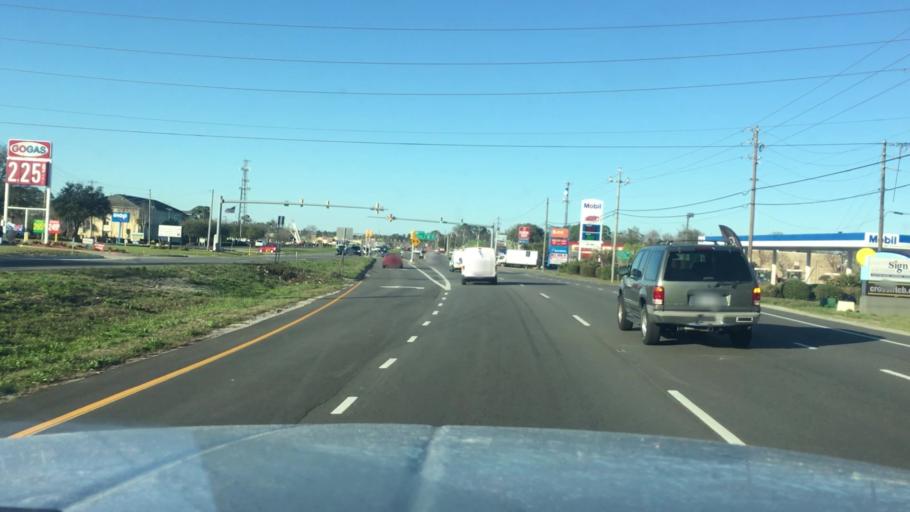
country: US
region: North Carolina
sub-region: New Hanover County
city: Myrtle Grove
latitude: 34.1335
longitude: -77.8951
